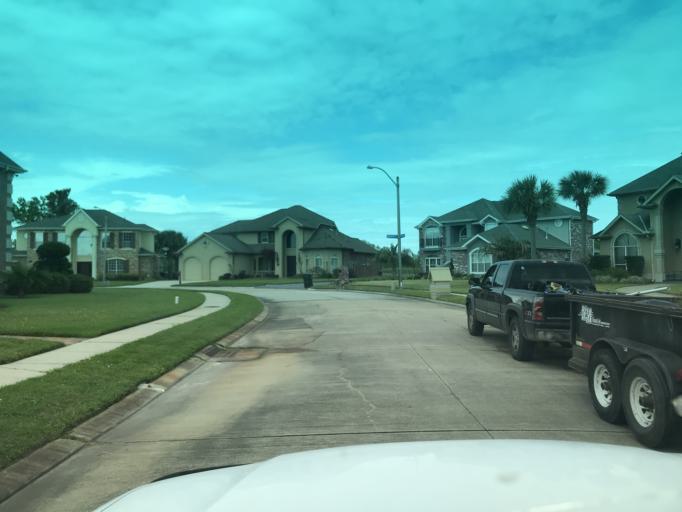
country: US
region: Louisiana
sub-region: Saint Bernard Parish
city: Chalmette
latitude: 30.0344
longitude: -89.9483
